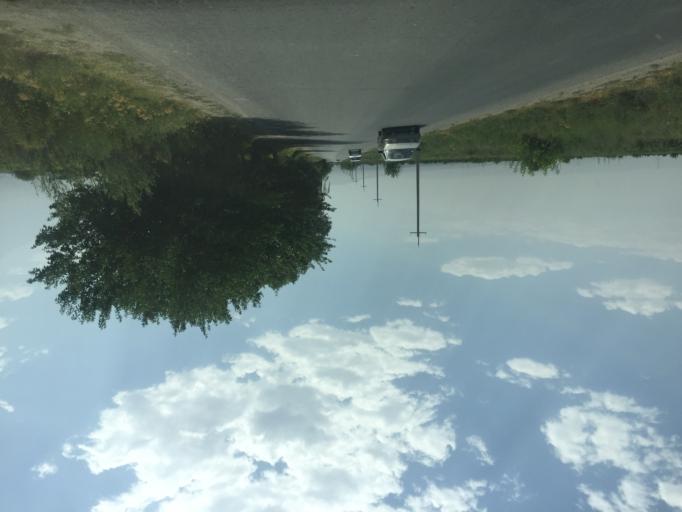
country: AM
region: Ararat
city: Shahumyan
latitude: 39.8881
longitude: 44.5931
